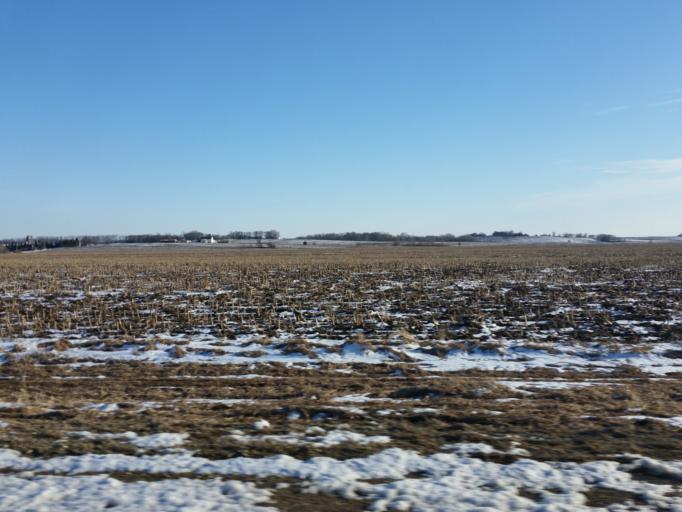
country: US
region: Minnesota
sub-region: Dakota County
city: Rosemount
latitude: 44.7029
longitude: -93.1429
